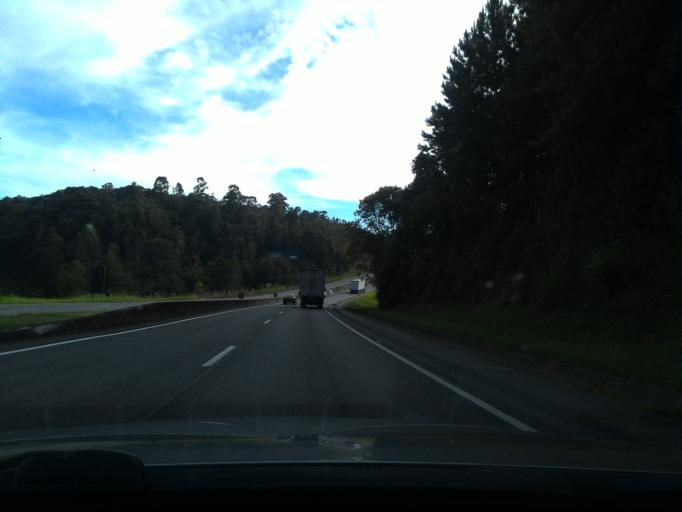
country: BR
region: Parana
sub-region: Campina Grande Do Sul
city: Campina Grande do Sul
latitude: -25.1937
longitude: -48.8888
